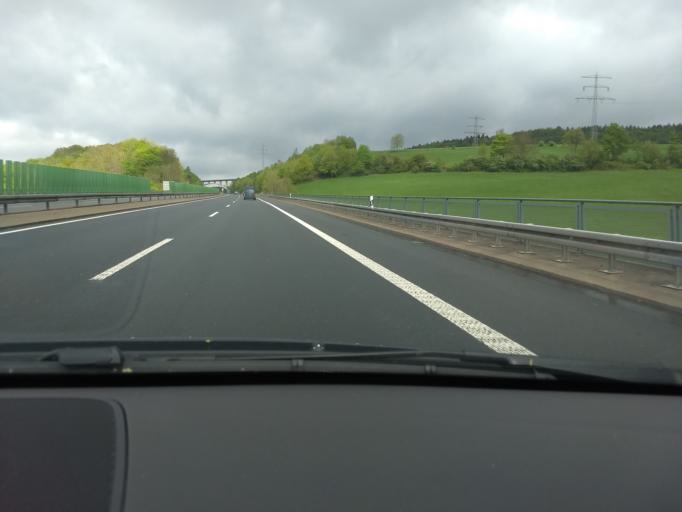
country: DE
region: North Rhine-Westphalia
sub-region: Regierungsbezirk Arnsberg
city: Arnsberg
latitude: 51.4088
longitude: 8.0803
